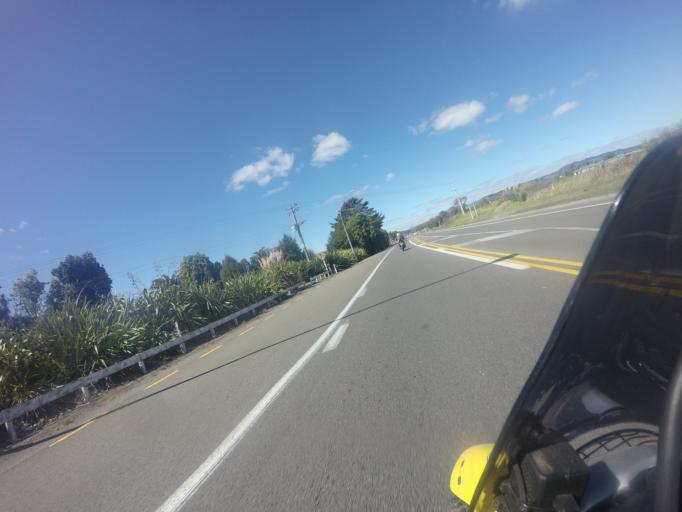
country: NZ
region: Bay of Plenty
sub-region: Whakatane District
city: Whakatane
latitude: -37.9485
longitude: 176.9372
